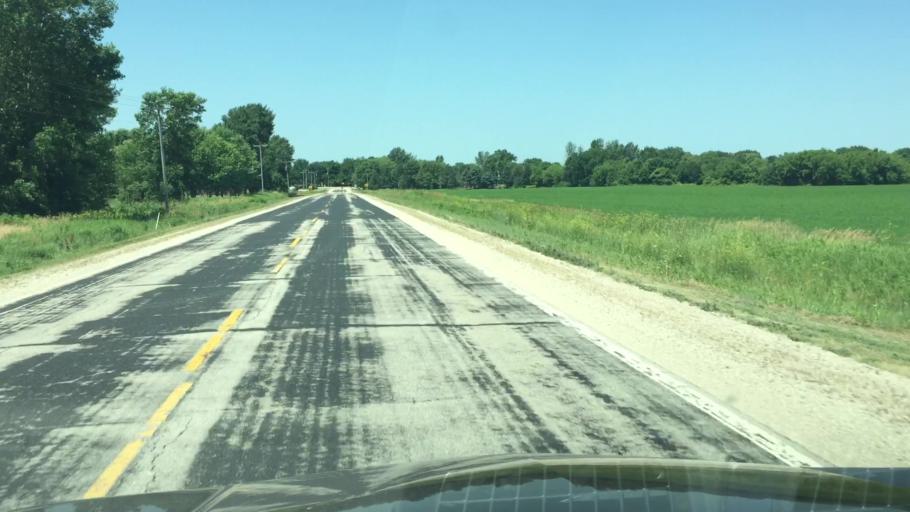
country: US
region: Wisconsin
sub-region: Fond du Lac County
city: Saint Peter
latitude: 43.9696
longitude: -88.3010
